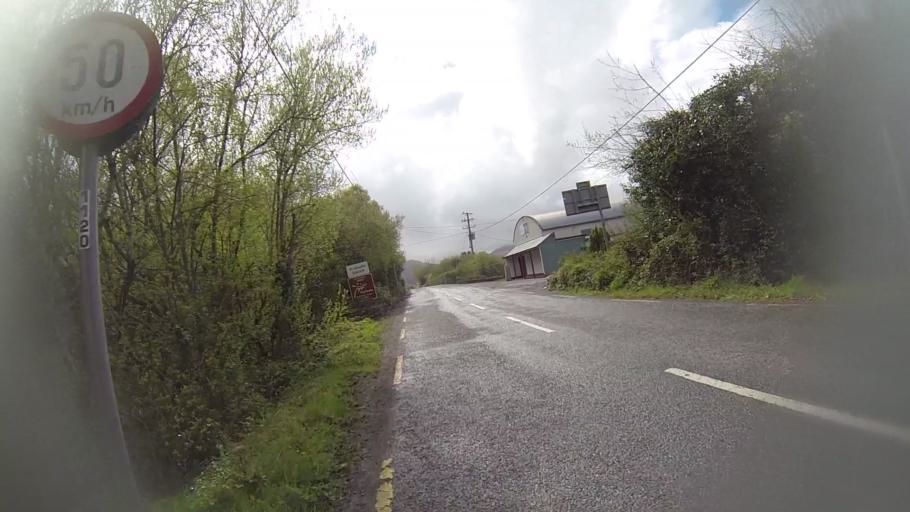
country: IE
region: Munster
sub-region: Ciarrai
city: Killorglin
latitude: 51.8395
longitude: -9.8951
